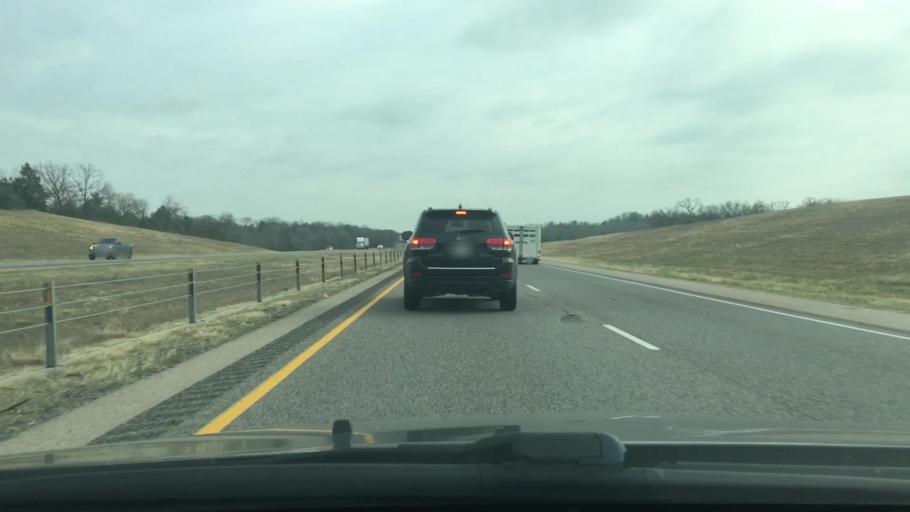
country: US
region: Texas
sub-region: Leon County
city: Buffalo
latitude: 31.5144
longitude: -96.1059
